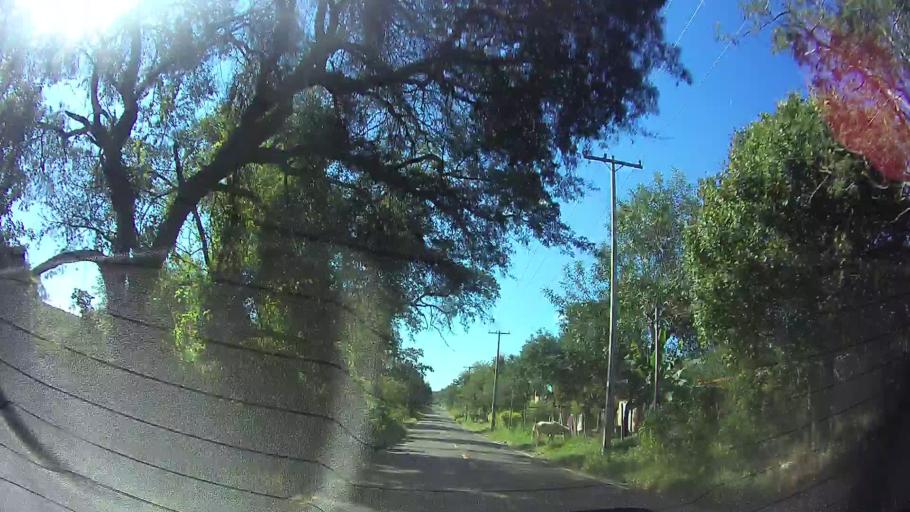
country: PY
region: Central
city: Limpio
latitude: -25.1984
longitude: -57.4779
